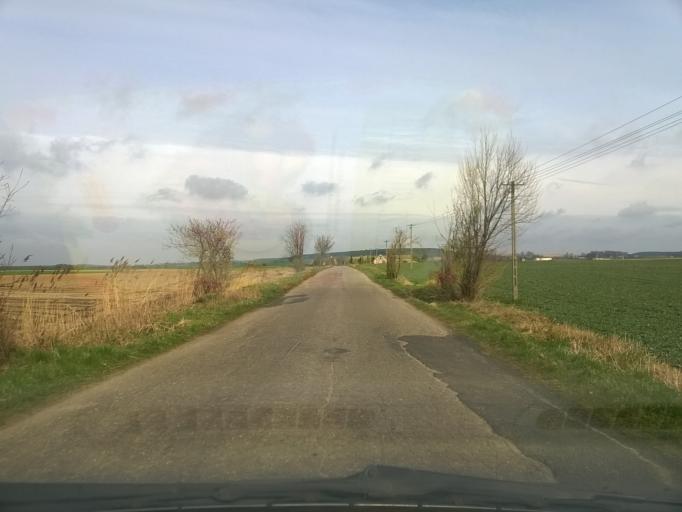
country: PL
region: Greater Poland Voivodeship
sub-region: Powiat wagrowiecki
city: Golancz
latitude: 52.9657
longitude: 17.3390
